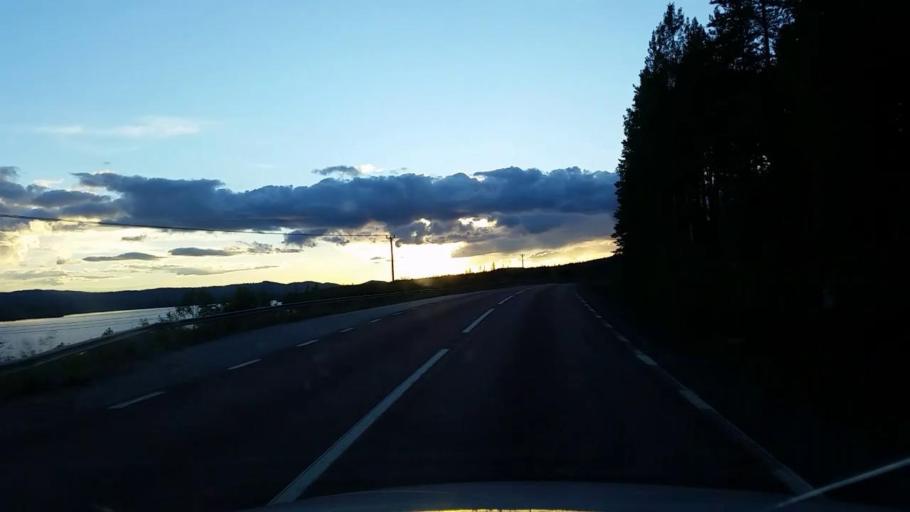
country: SE
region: Gaevleborg
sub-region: Ljusdals Kommun
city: Farila
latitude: 62.1032
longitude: 15.7769
